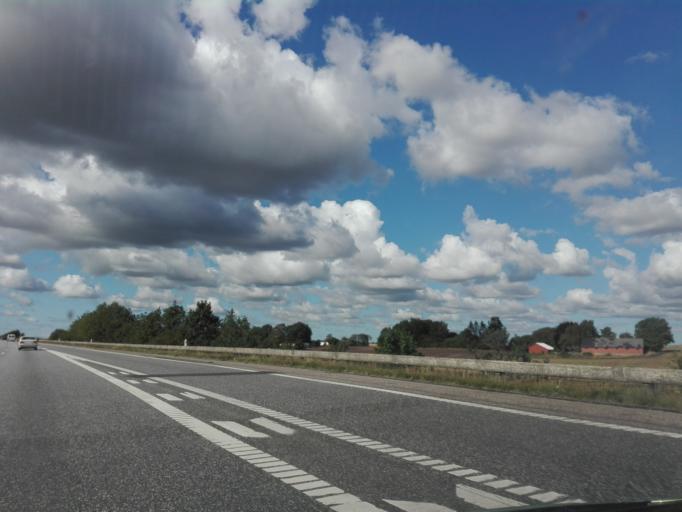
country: DK
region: North Denmark
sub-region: Mariagerfjord Kommune
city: Hobro
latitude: 56.5738
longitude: 9.8449
